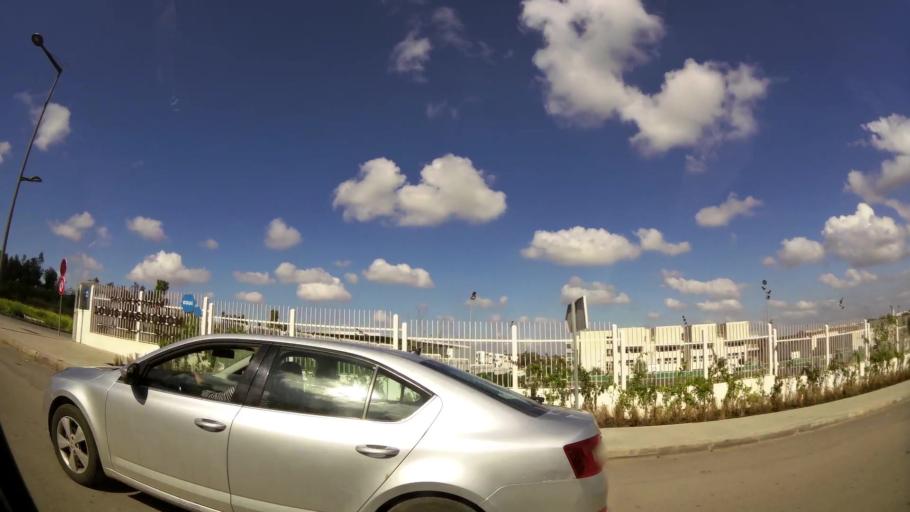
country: MA
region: Grand Casablanca
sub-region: Nouaceur
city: Bouskoura
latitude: 33.4788
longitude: -7.6221
